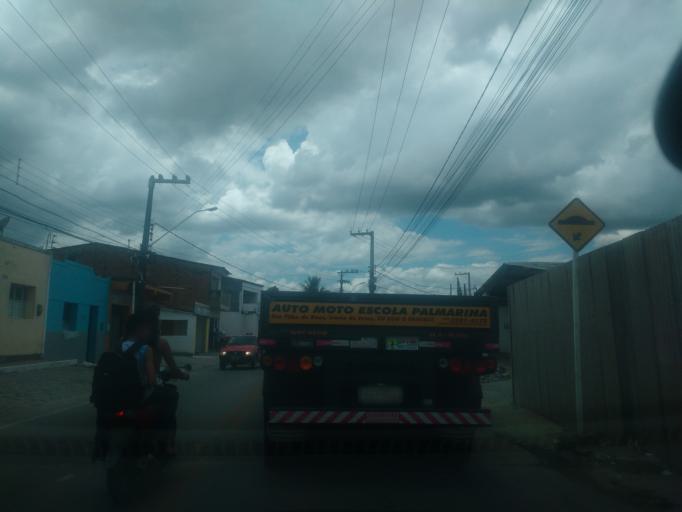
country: BR
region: Alagoas
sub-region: Uniao Dos Palmares
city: Uniao dos Palmares
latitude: -9.1539
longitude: -36.0230
